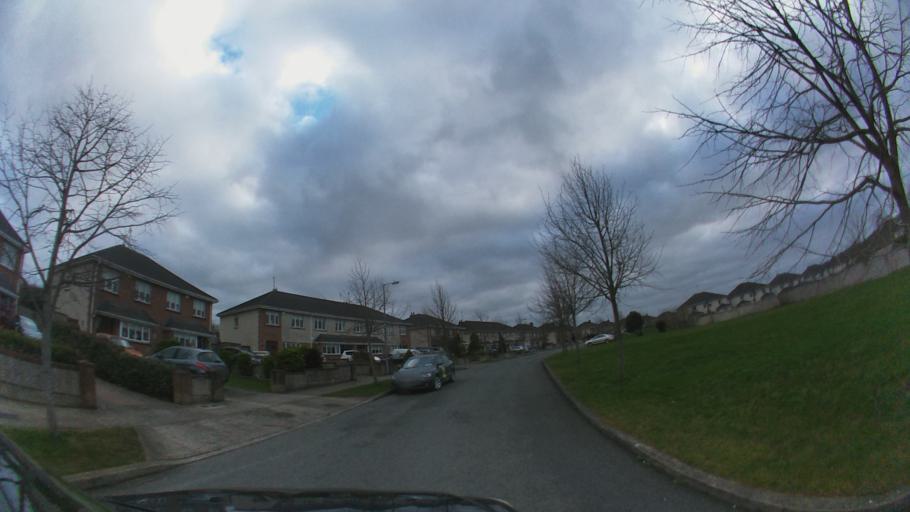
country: IE
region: Leinster
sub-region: An Mhi
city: Duleek
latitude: 53.6924
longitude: -6.4127
